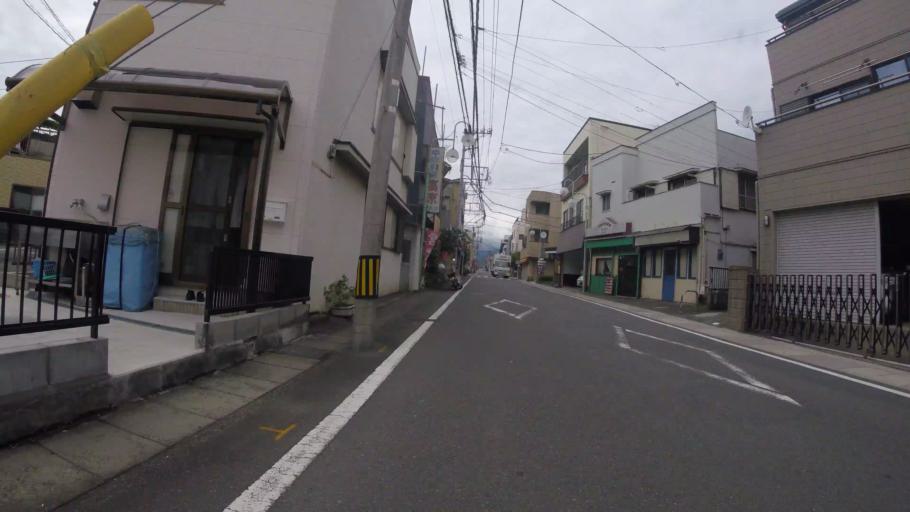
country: JP
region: Shizuoka
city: Mishima
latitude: 35.1209
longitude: 138.9102
